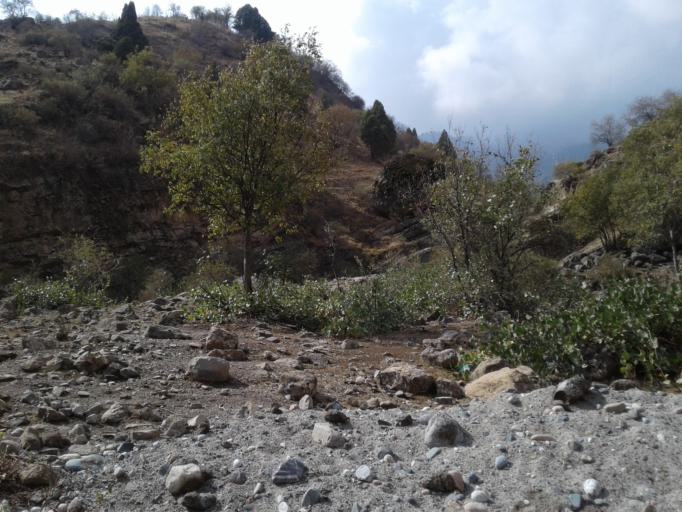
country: TJ
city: Shahrinav
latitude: 38.7119
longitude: 68.3694
